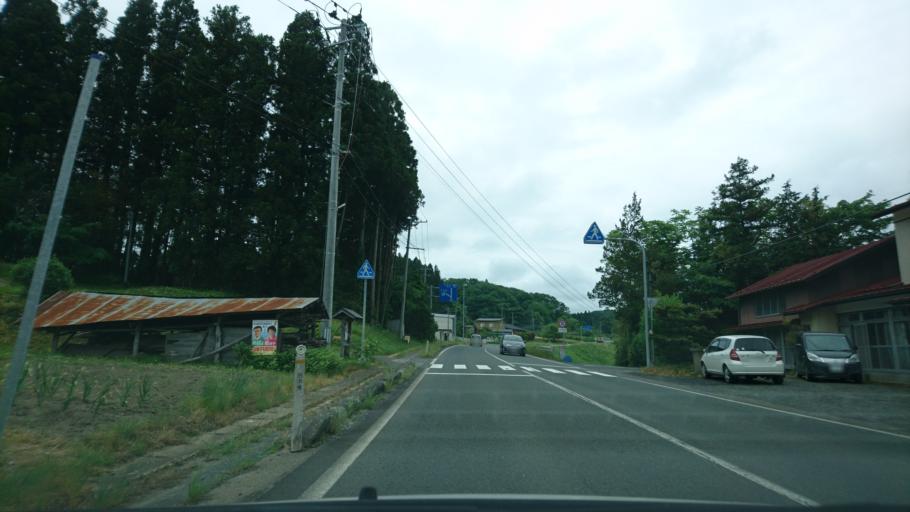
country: JP
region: Iwate
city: Ichinoseki
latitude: 38.8918
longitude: 141.1213
